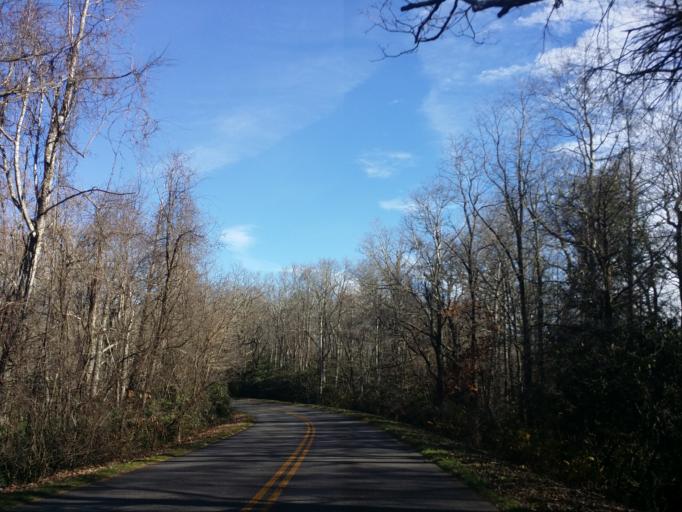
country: US
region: North Carolina
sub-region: Mitchell County
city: Spruce Pine
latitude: 35.7940
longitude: -82.1629
